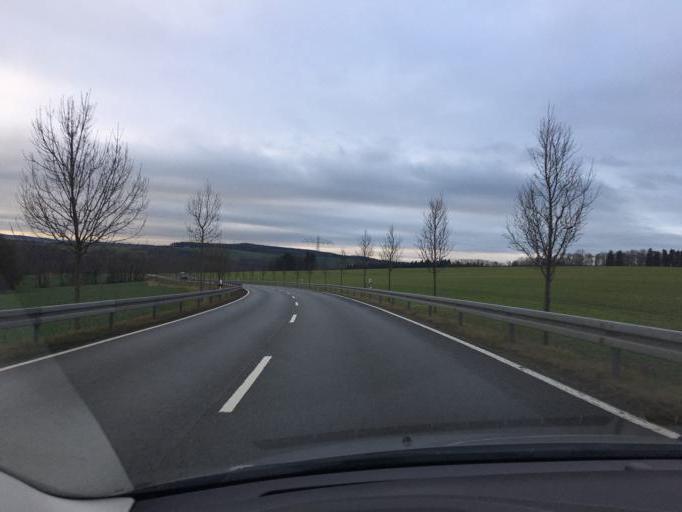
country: DE
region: Thuringia
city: Juckelberg
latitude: 50.9091
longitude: 12.6477
